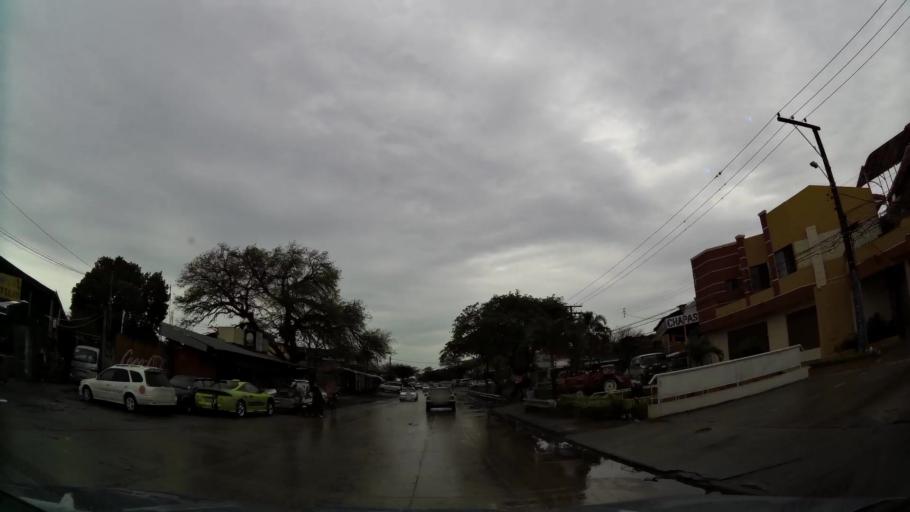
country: BO
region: Santa Cruz
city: Santa Cruz de la Sierra
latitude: -17.8109
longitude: -63.1942
